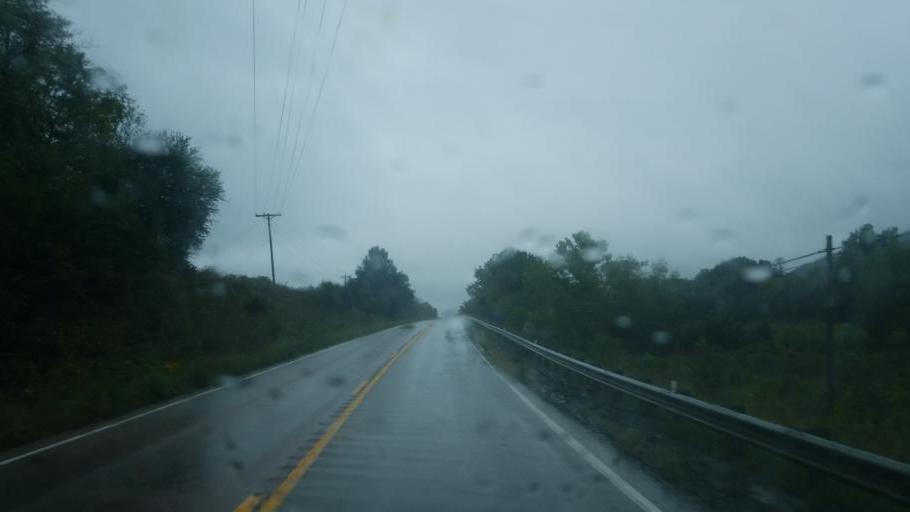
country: US
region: Kentucky
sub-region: Fleming County
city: Flemingsburg
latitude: 38.3449
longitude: -83.6009
